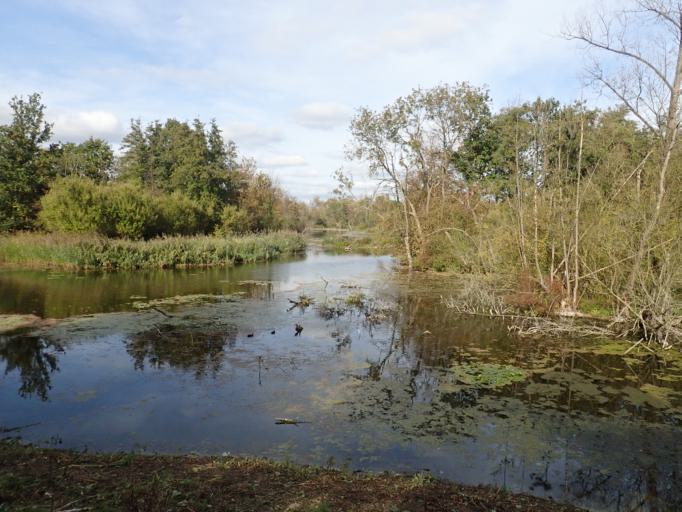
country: BE
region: Flanders
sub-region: Provincie Antwerpen
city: Hemiksem
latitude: 51.1340
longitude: 4.3055
